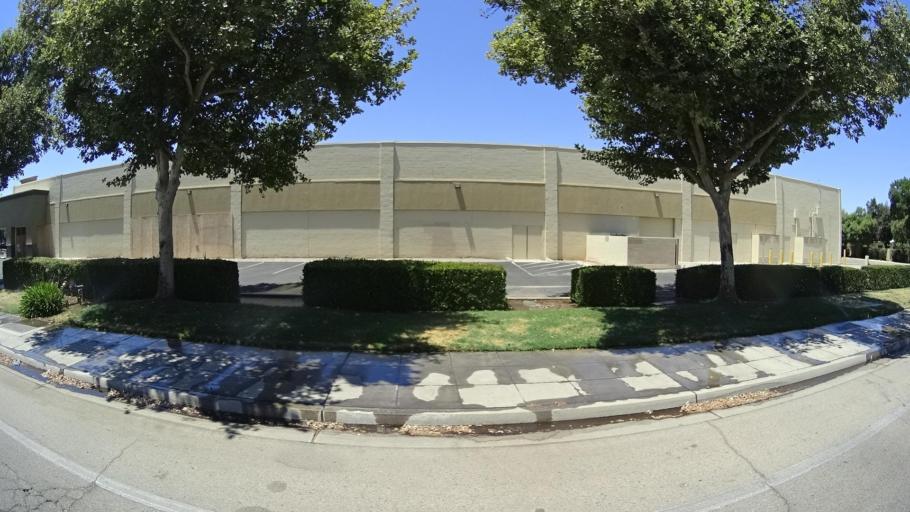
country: US
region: California
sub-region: Fresno County
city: Sunnyside
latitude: 36.7380
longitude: -119.7274
